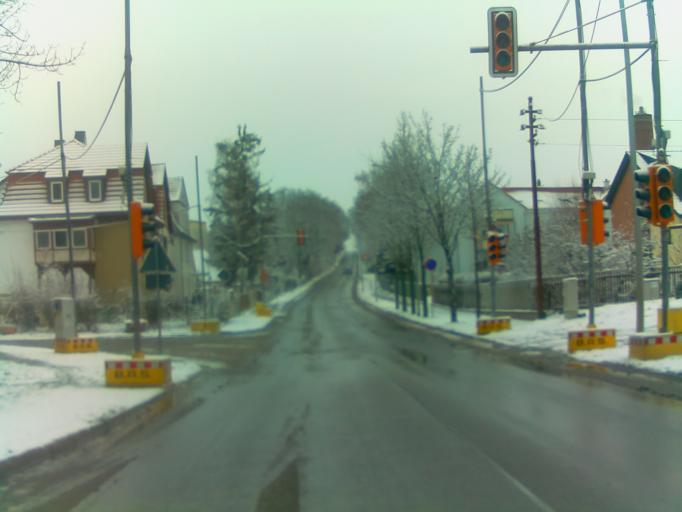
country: DE
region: Thuringia
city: Arnstadt
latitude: 50.8318
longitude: 10.9597
